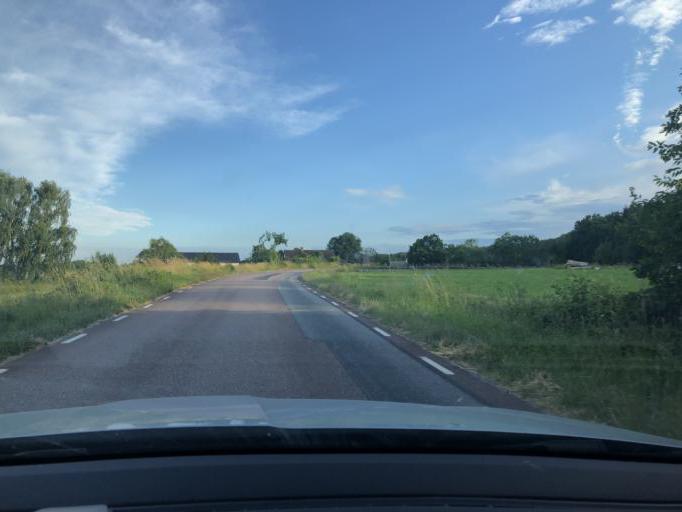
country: SE
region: Blekinge
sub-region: Solvesborgs Kommun
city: Soelvesborg
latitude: 56.1368
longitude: 14.6077
